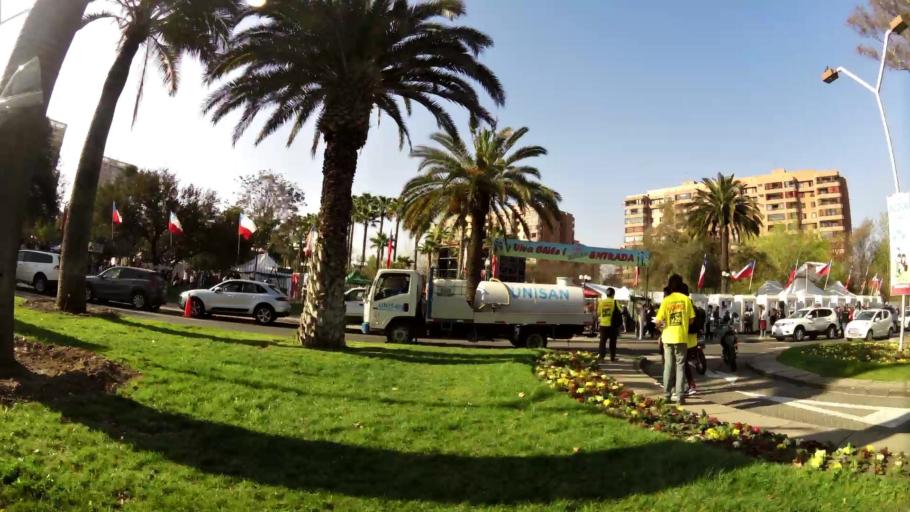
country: CL
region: Santiago Metropolitan
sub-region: Provincia de Santiago
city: Villa Presidente Frei, Nunoa, Santiago, Chile
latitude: -33.4419
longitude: -70.6114
